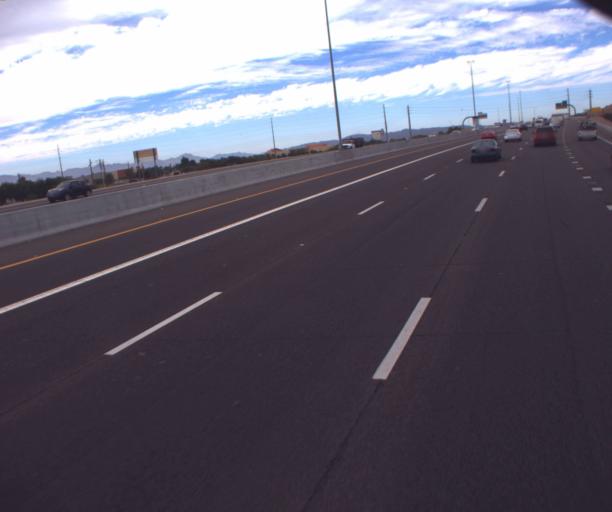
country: US
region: Arizona
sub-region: Maricopa County
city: Chandler
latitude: 33.2843
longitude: -111.8310
